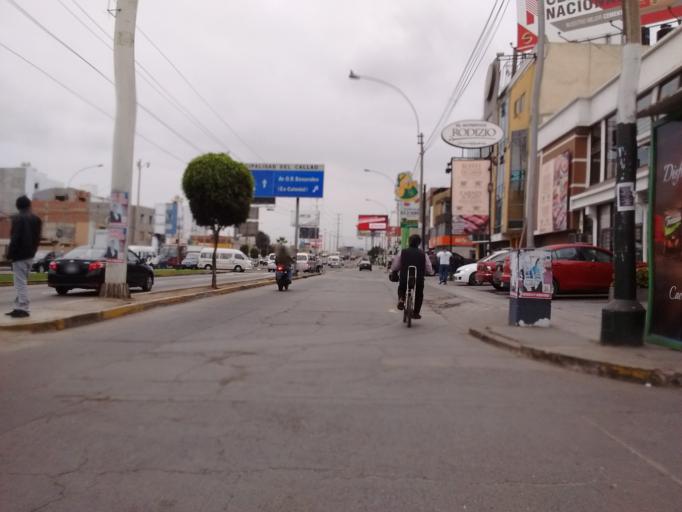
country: PE
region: Callao
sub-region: Callao
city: Callao
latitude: -12.0564
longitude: -77.0975
